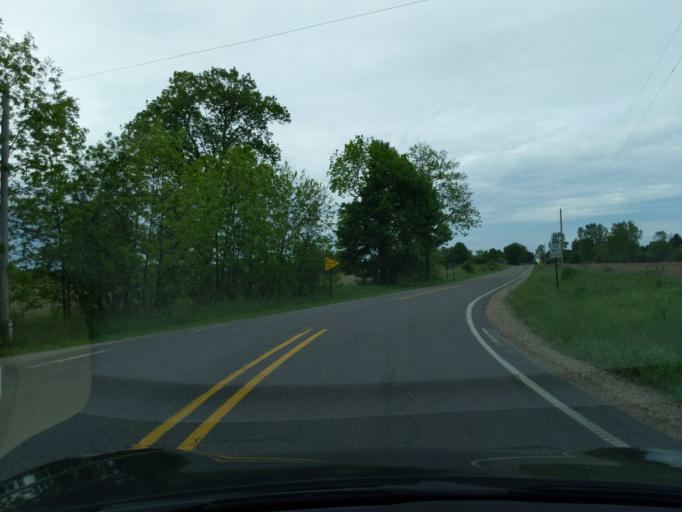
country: US
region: Michigan
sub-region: Ingham County
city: Leslie
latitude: 42.4682
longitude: -84.3560
